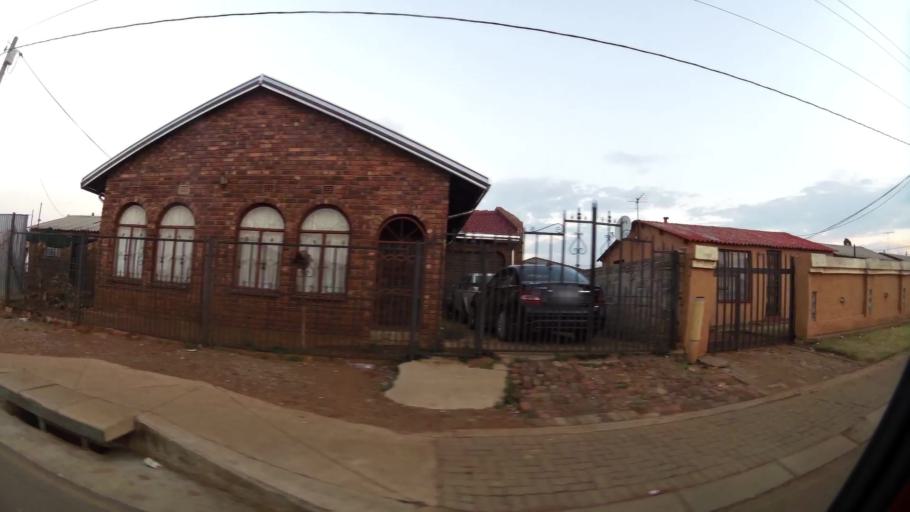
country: ZA
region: Gauteng
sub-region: City of Johannesburg Metropolitan Municipality
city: Orange Farm
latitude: -26.5572
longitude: 27.8691
